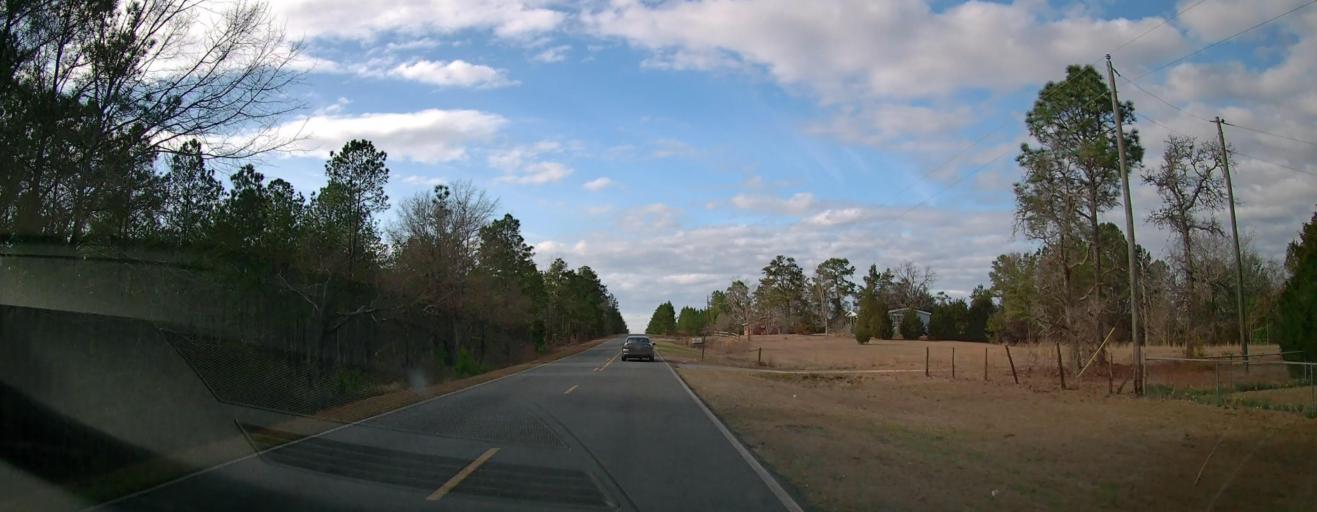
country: US
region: Georgia
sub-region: Talbot County
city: Talbotton
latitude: 32.5092
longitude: -84.5897
